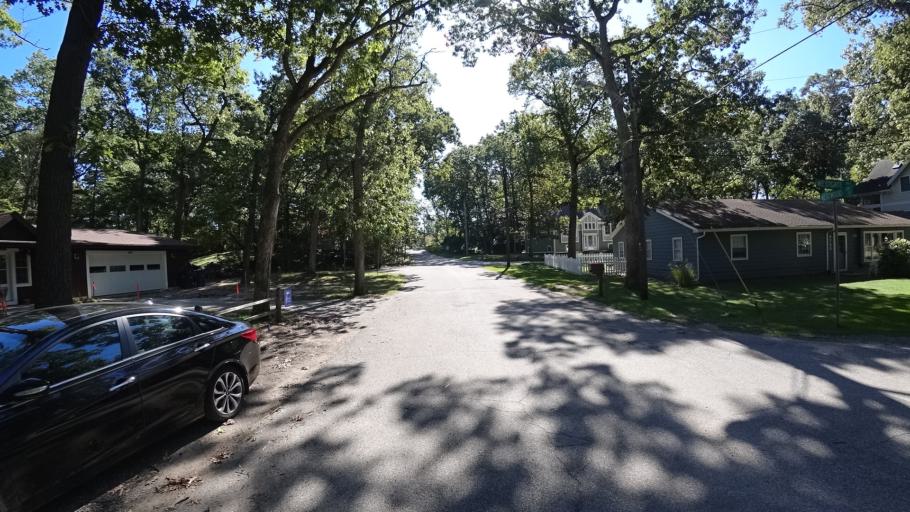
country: US
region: Indiana
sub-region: LaPorte County
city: Long Beach
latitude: 41.7518
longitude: -86.8355
